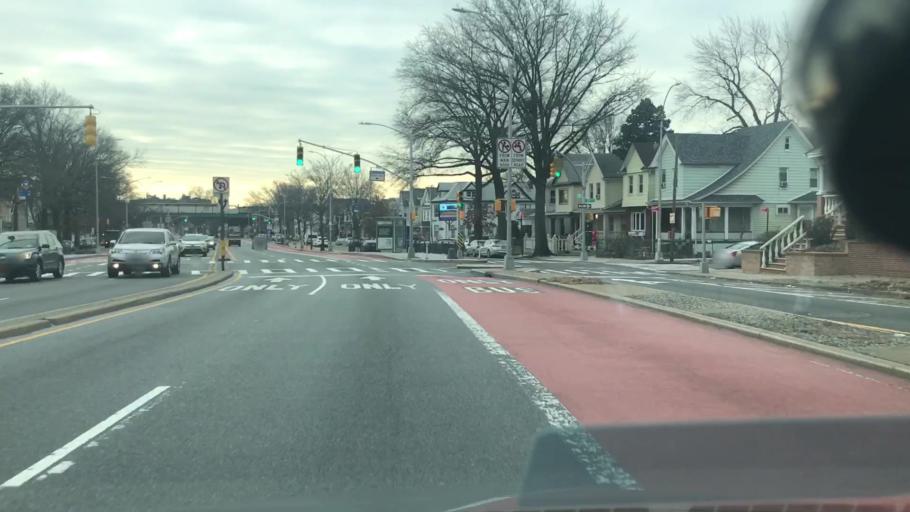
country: US
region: New York
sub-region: Queens County
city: Borough of Queens
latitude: 40.6965
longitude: -73.8529
